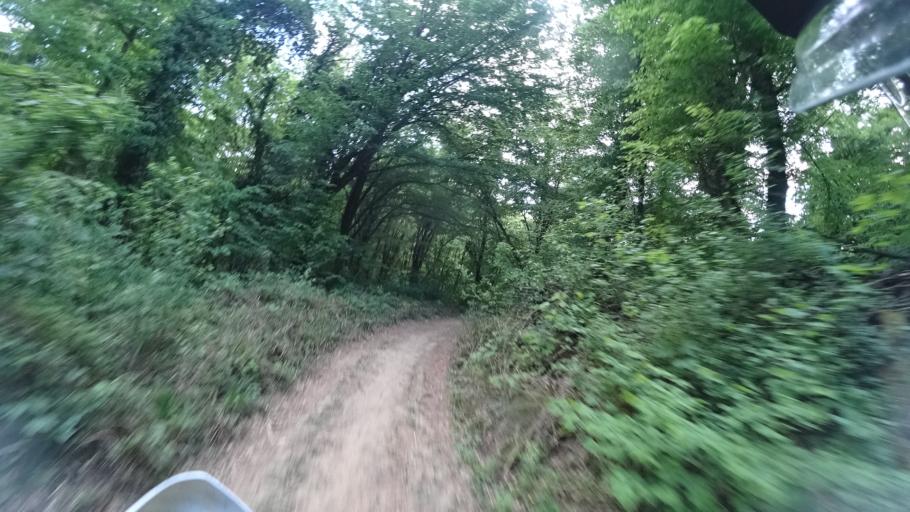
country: HR
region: Grad Zagreb
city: Stenjevec
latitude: 45.8459
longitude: 15.8946
